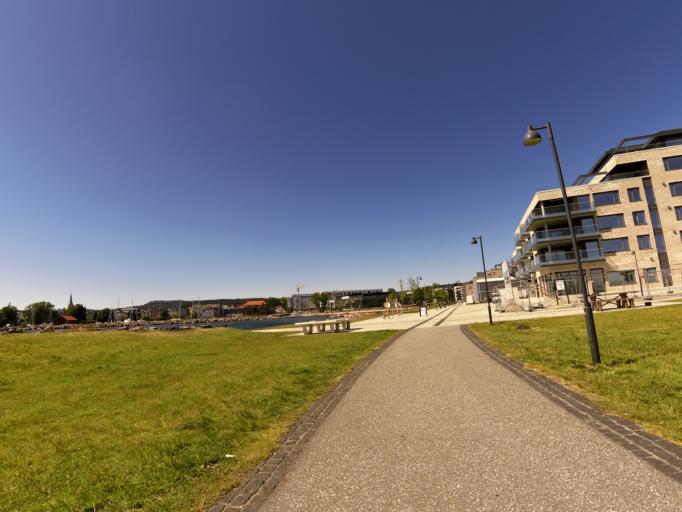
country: NO
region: Vest-Agder
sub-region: Kristiansand
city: Kristiansand
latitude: 58.1439
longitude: 8.0101
